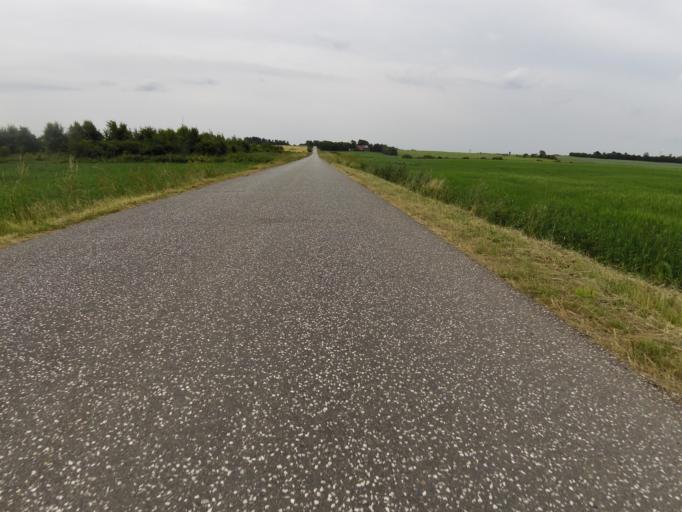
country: DK
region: Central Jutland
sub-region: Holstebro Kommune
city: Holstebro
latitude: 56.4172
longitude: 8.6730
